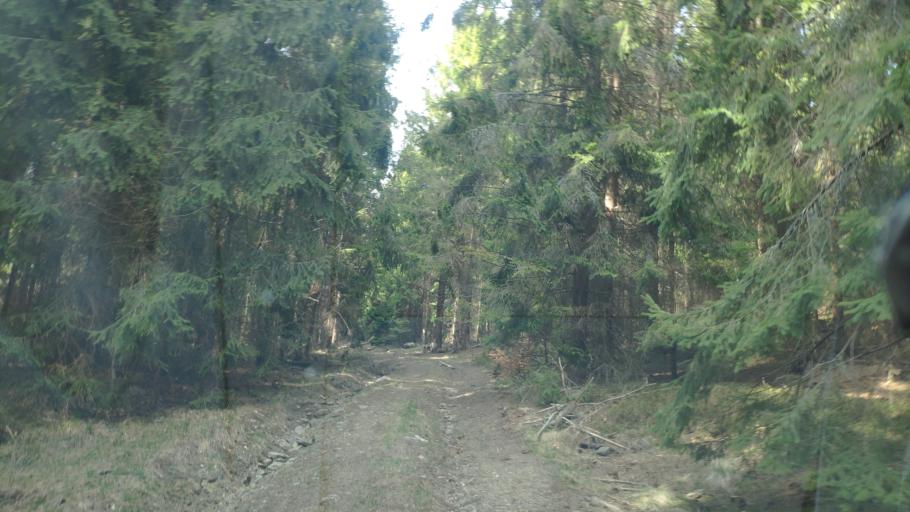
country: SK
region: Kosicky
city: Gelnica
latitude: 48.7581
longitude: 21.0195
